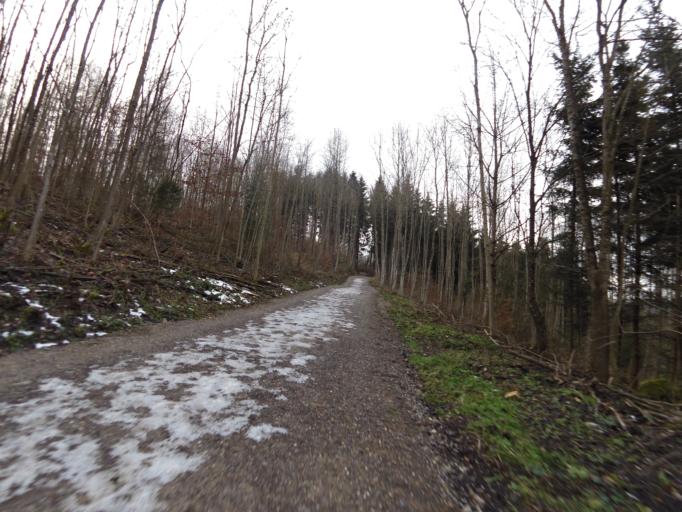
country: CH
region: Zurich
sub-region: Bezirk Dietikon
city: Schlieren / Boden
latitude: 47.3864
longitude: 8.4622
